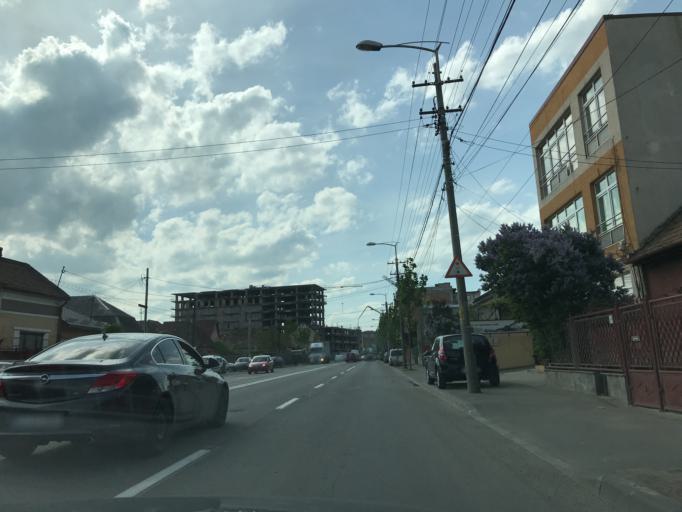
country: RO
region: Cluj
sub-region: Municipiul Cluj-Napoca
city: Cluj-Napoca
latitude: 46.7884
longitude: 23.6180
